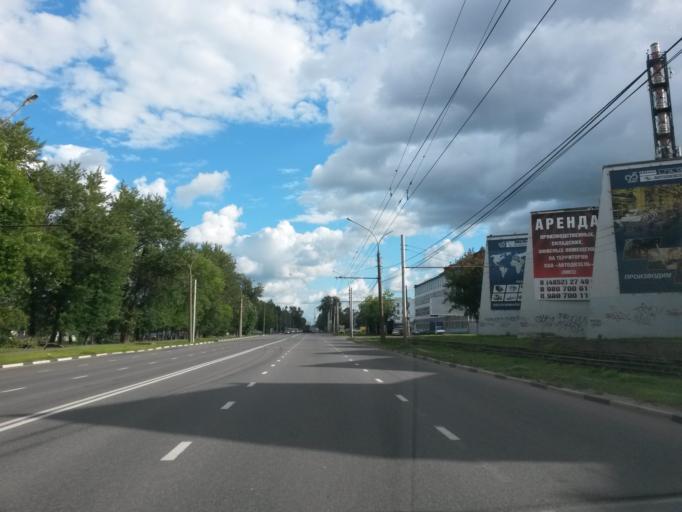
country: RU
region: Jaroslavl
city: Yaroslavl
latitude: 57.6505
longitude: 39.8476
